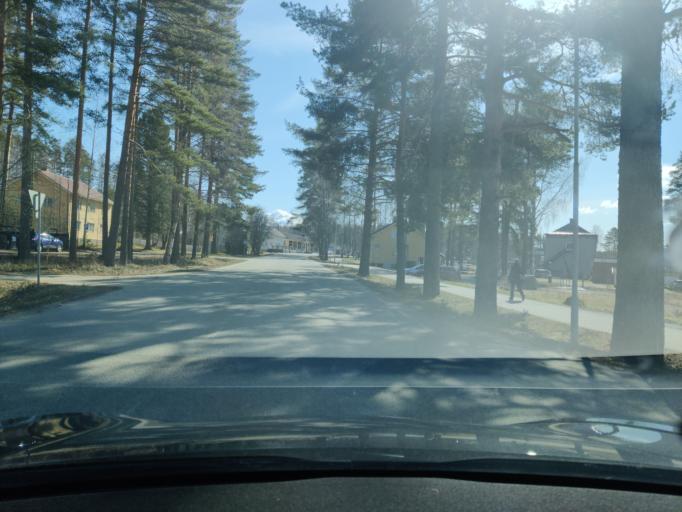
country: FI
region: Northern Savo
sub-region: Kuopio
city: Vehmersalmi
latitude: 62.7625
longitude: 28.0244
